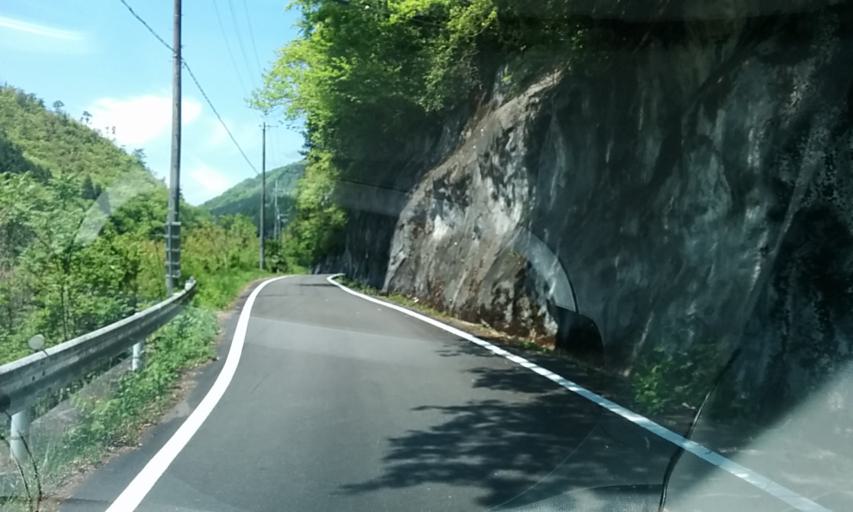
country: JP
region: Kyoto
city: Ayabe
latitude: 35.2214
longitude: 135.2970
